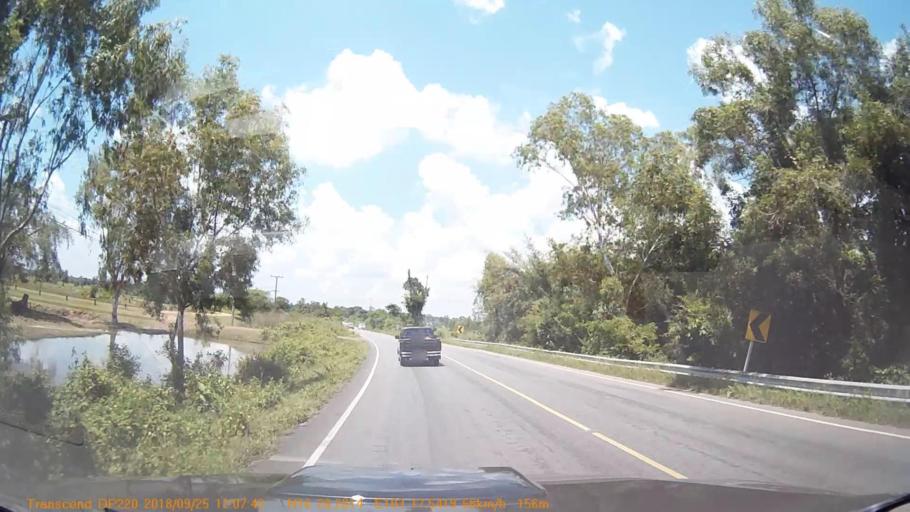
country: TH
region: Kalasin
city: Yang Talat
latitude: 16.4381
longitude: 103.2923
